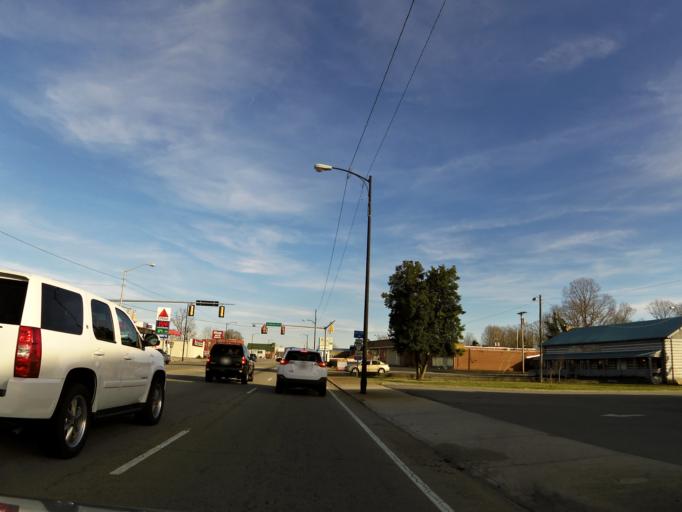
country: US
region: Tennessee
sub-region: White County
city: Sparta
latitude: 35.9316
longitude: -85.4759
